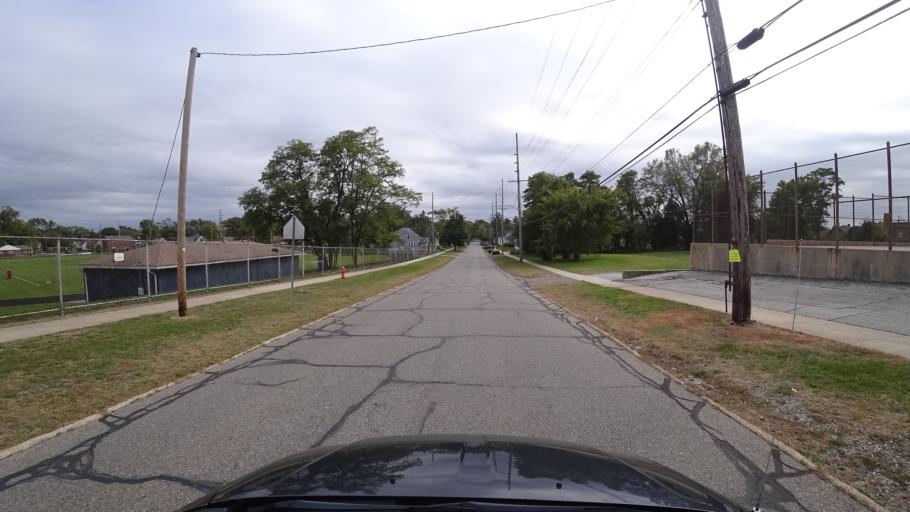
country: US
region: Indiana
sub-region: LaPorte County
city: Michigan City
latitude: 41.7088
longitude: -86.8960
